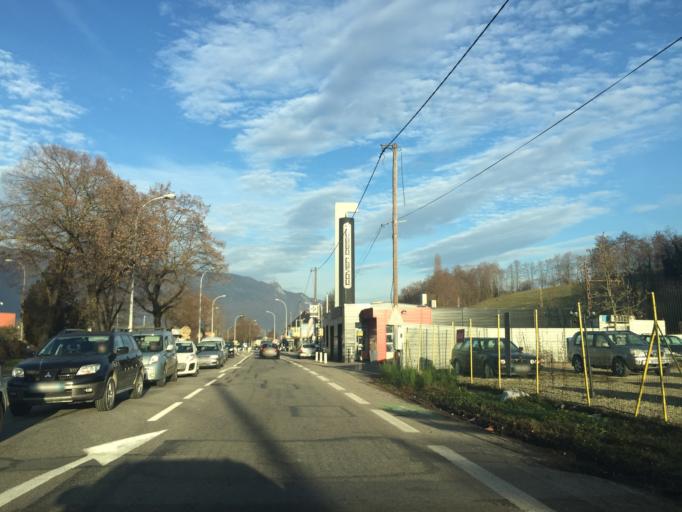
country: FR
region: Rhone-Alpes
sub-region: Departement de la Savoie
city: La Motte-Servolex
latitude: 45.5915
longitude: 5.9032
